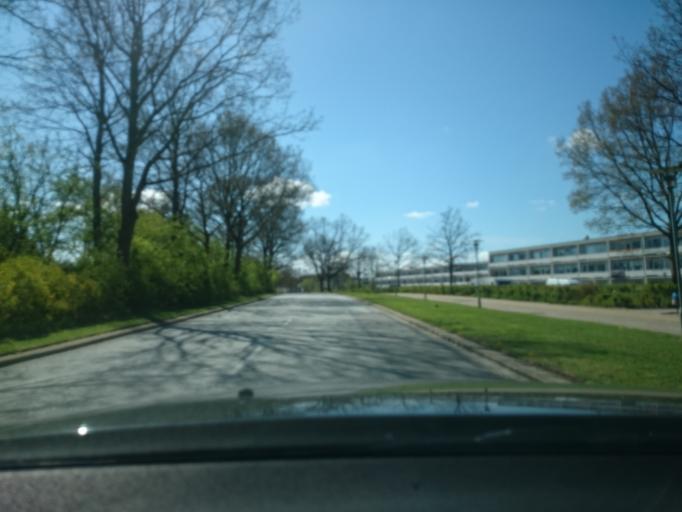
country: DK
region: Capital Region
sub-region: Lyngby-Tarbaek Kommune
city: Kongens Lyngby
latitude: 55.7921
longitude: 12.5344
